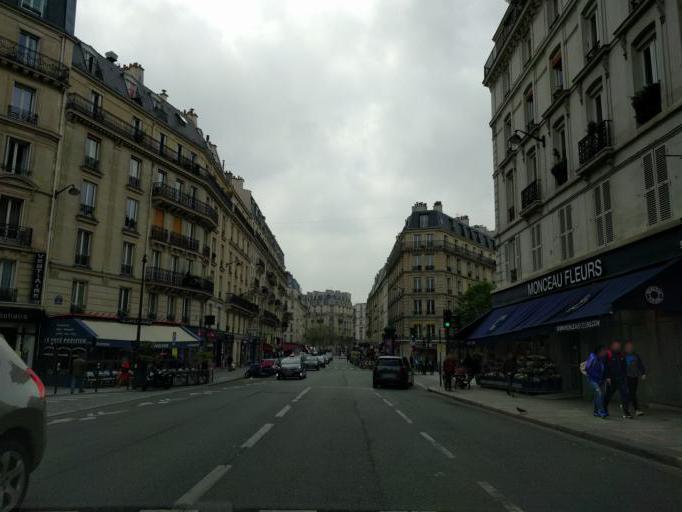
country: FR
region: Ile-de-France
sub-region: Paris
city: Paris
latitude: 48.8402
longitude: 2.3515
